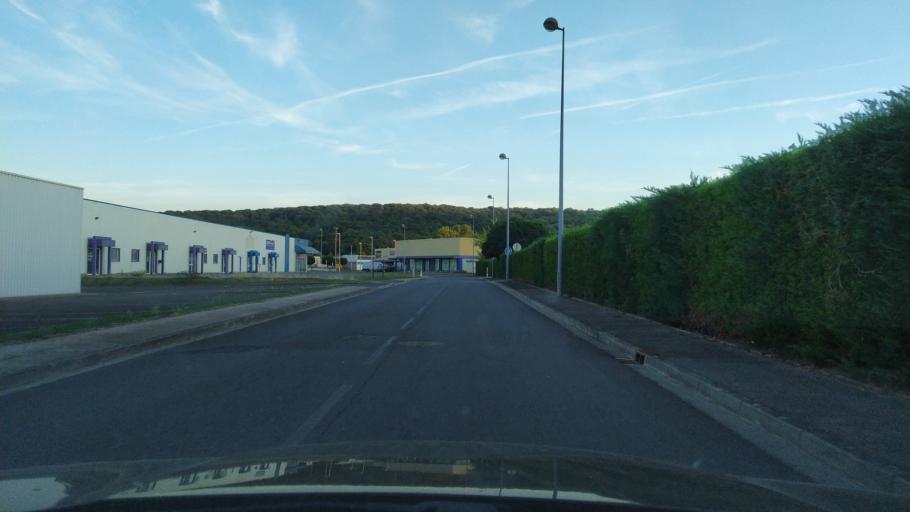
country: FR
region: Lorraine
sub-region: Departement de la Moselle
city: Jouy-aux-Arches
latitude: 49.0778
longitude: 6.0958
